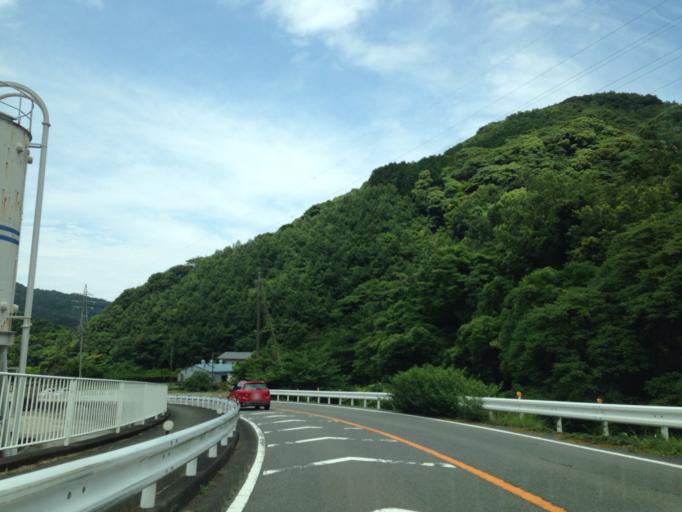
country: JP
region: Shizuoka
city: Heda
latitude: 34.9062
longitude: 138.8156
